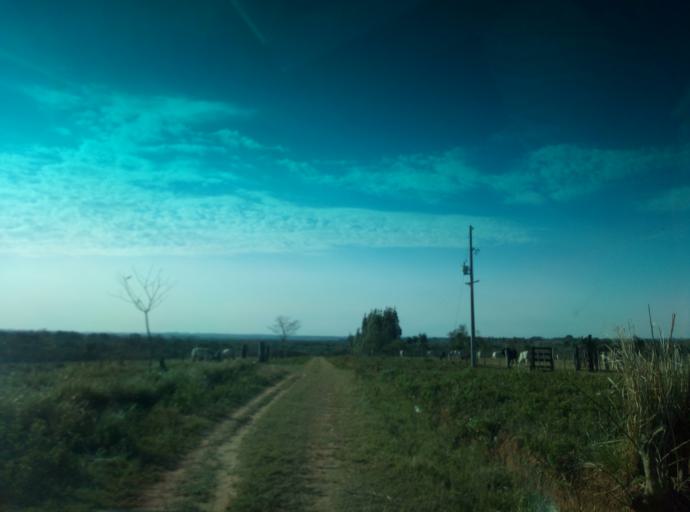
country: PY
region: Caaguazu
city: Doctor Cecilio Baez
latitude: -25.1622
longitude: -56.2321
